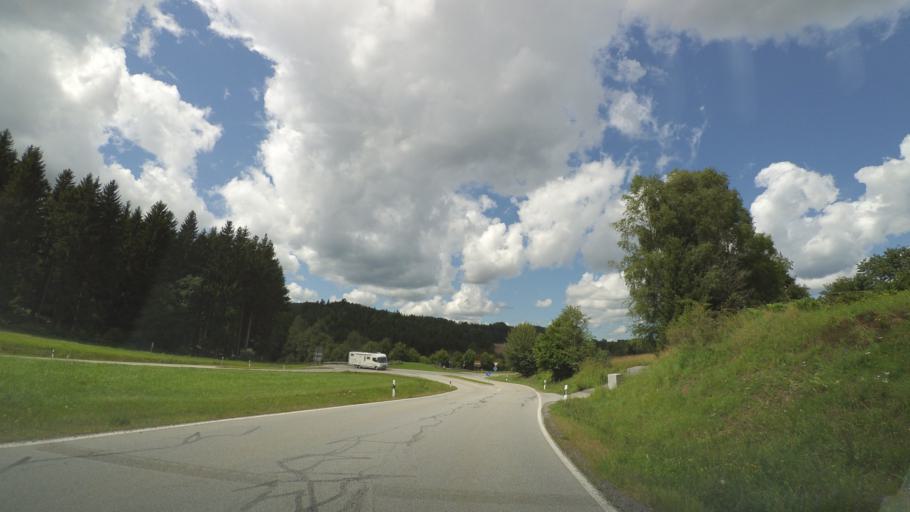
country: DE
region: Bavaria
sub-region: Lower Bavaria
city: Bodenmais
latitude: 49.0642
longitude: 13.0859
